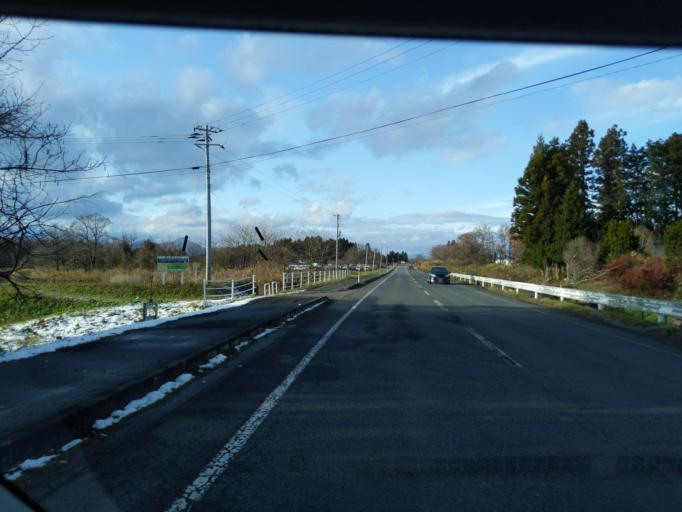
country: JP
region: Iwate
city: Mizusawa
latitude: 39.1915
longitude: 141.0723
